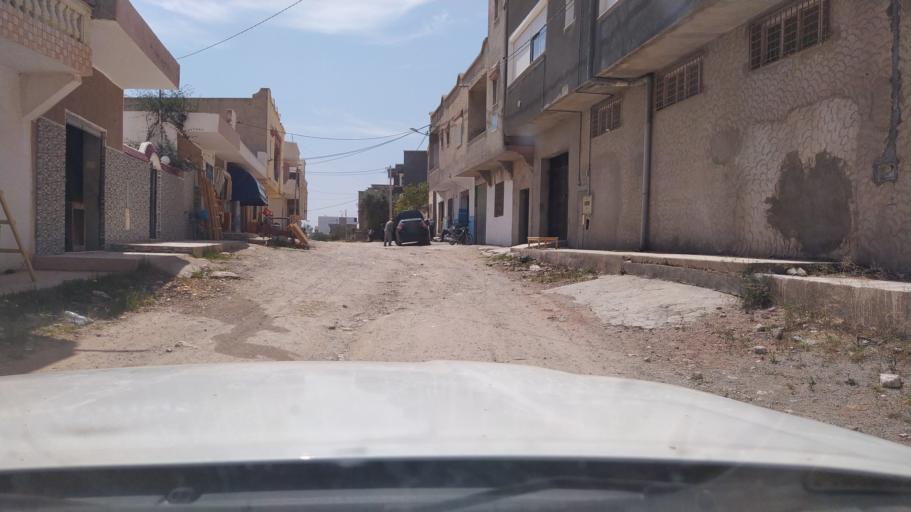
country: TN
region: Al Mahdiyah
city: Zouila
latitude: 35.5058
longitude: 11.0354
